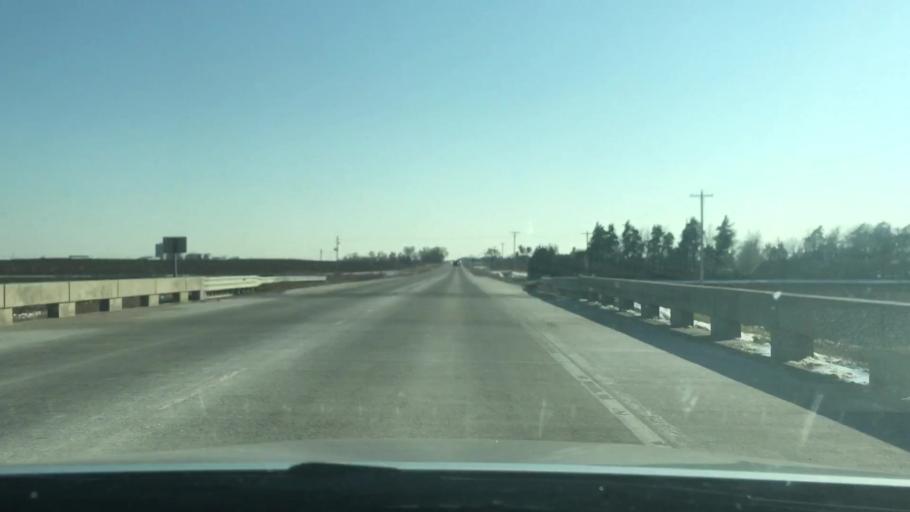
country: US
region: Kansas
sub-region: Rice County
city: Lyons
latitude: 38.3063
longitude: -98.2019
